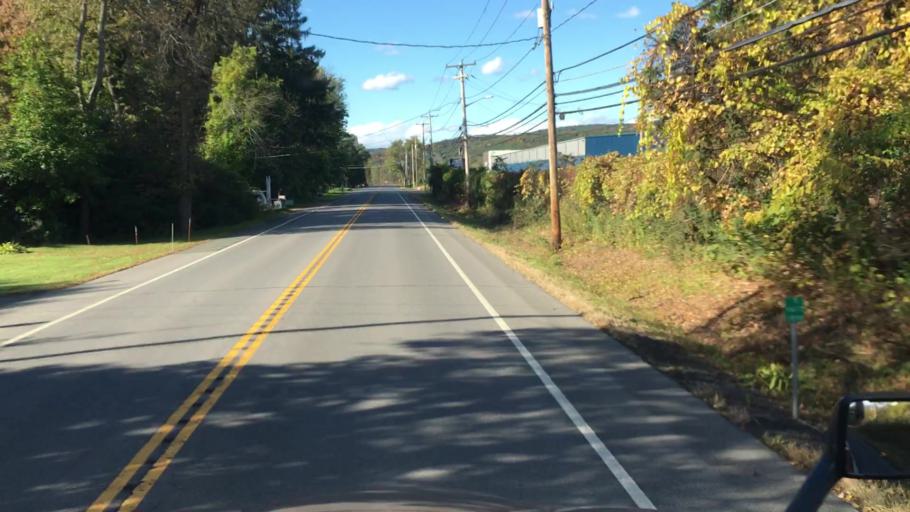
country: US
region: New York
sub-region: Schenectady County
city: Scotia
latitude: 42.8447
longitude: -73.9975
